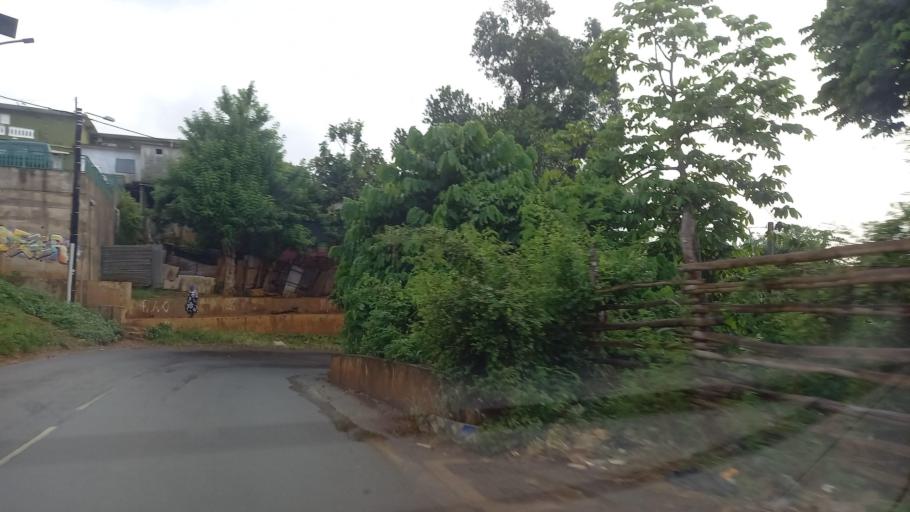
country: YT
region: Ouangani
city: Ouangani
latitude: -12.8366
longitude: 45.1587
